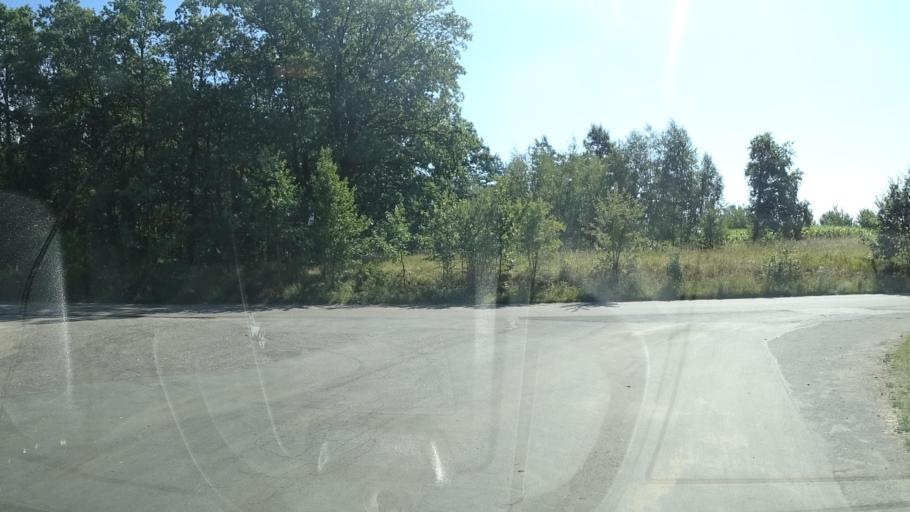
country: PL
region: Greater Poland Voivodeship
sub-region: Powiat koninski
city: Slesin
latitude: 52.3746
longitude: 18.3222
